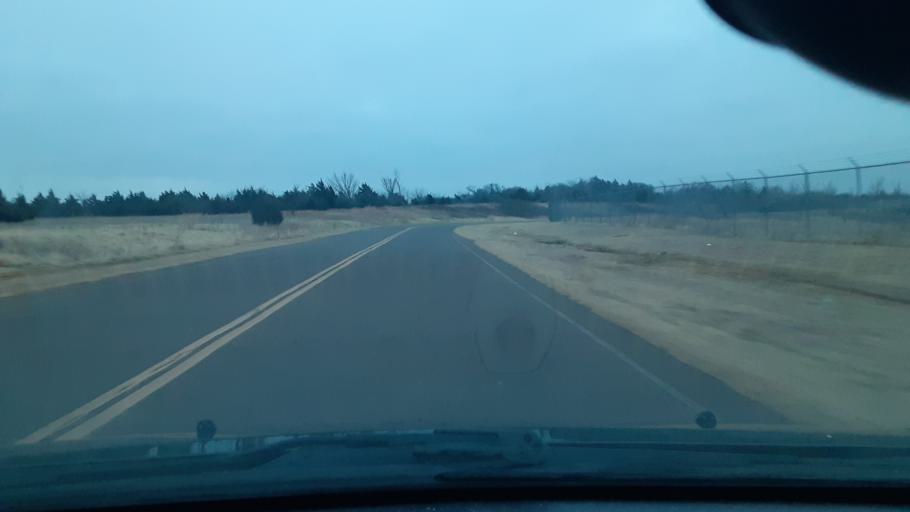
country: US
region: Oklahoma
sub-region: Logan County
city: Guthrie
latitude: 35.8619
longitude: -97.4176
